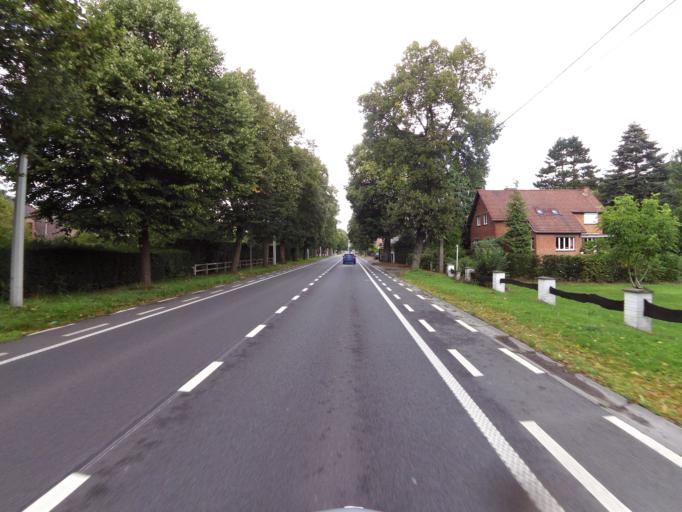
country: BE
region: Wallonia
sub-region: Province du Hainaut
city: Mons
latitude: 50.4440
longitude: 3.9859
